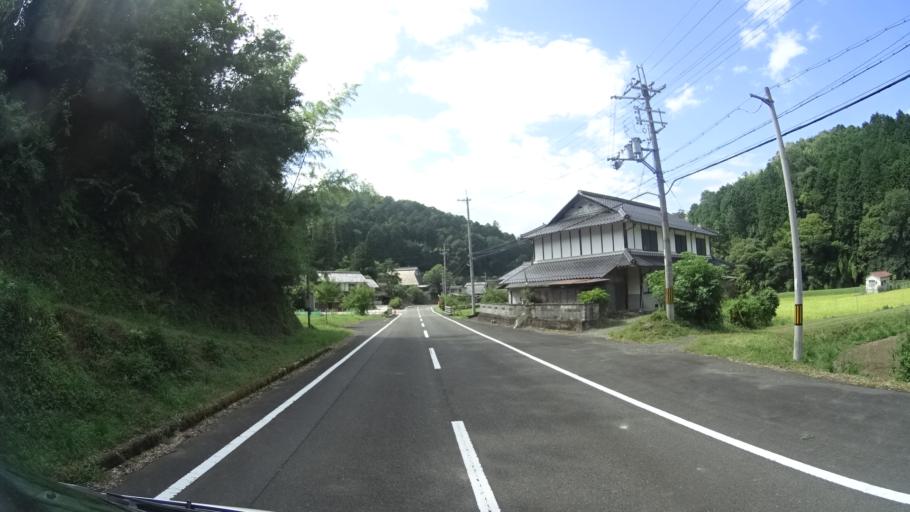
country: JP
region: Kyoto
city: Fukuchiyama
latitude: 35.3680
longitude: 135.1621
